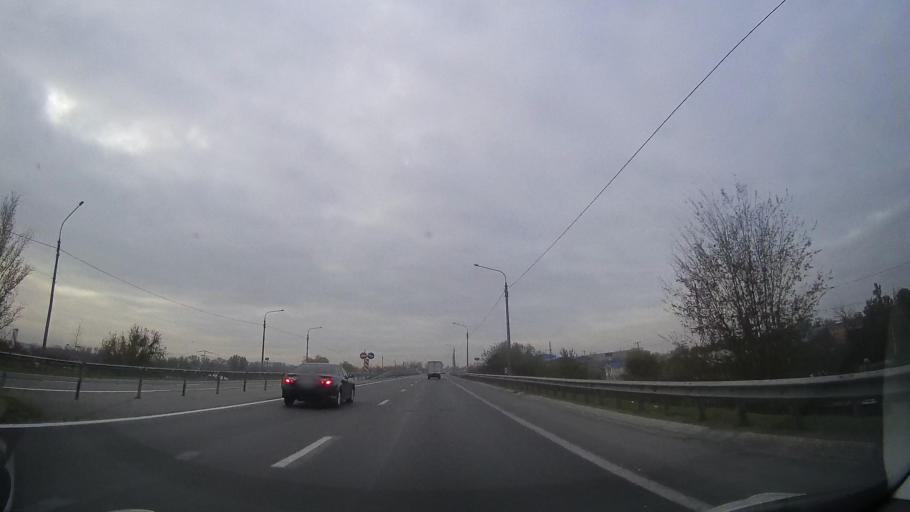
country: RU
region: Rostov
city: Bataysk
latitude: 47.1210
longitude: 39.7715
